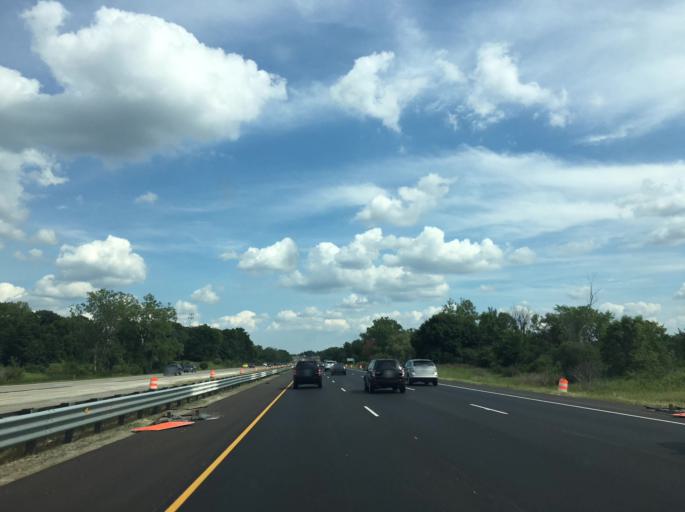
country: US
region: Michigan
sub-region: Oakland County
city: Waterford
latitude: 42.7183
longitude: -83.3458
